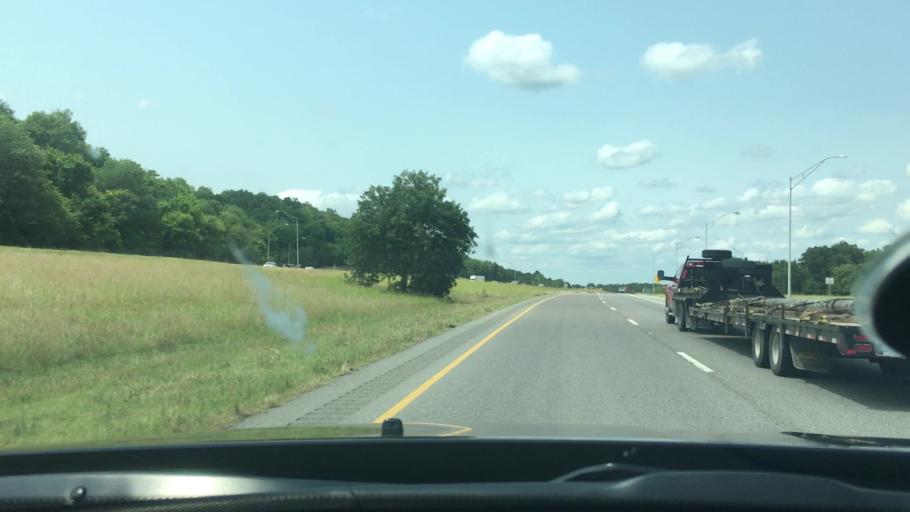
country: US
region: Oklahoma
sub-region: Murray County
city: Davis
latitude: 34.4745
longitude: -97.1556
